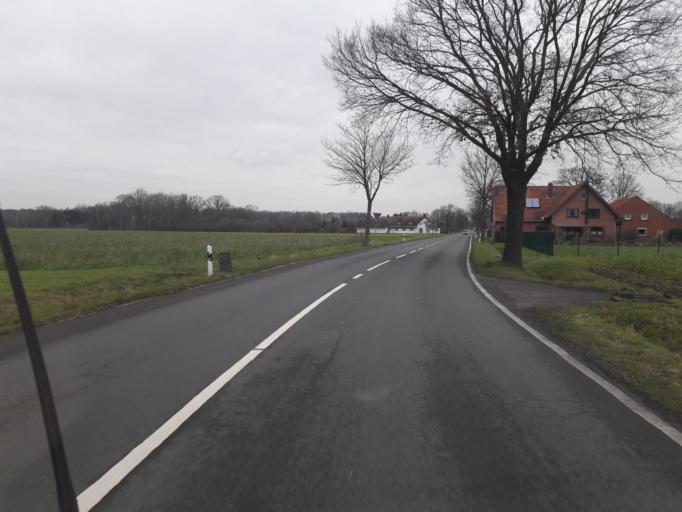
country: DE
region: Lower Saxony
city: Warmsen
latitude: 52.3875
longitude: 8.8519
